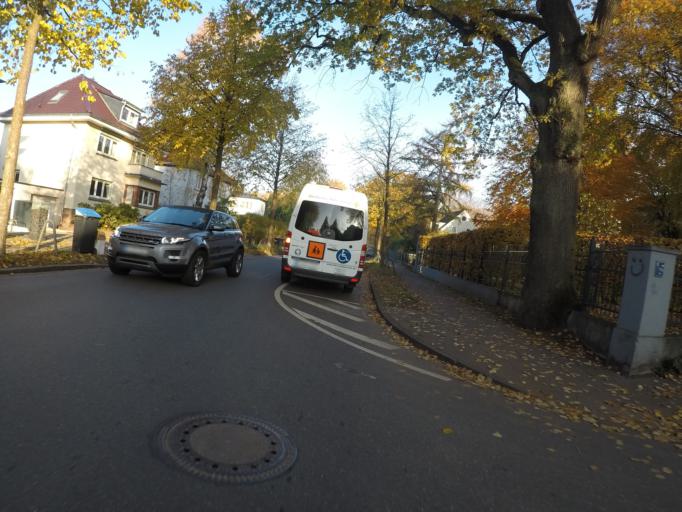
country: DE
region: Hamburg
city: Hamburg-Nord
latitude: 53.5960
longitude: 9.9589
